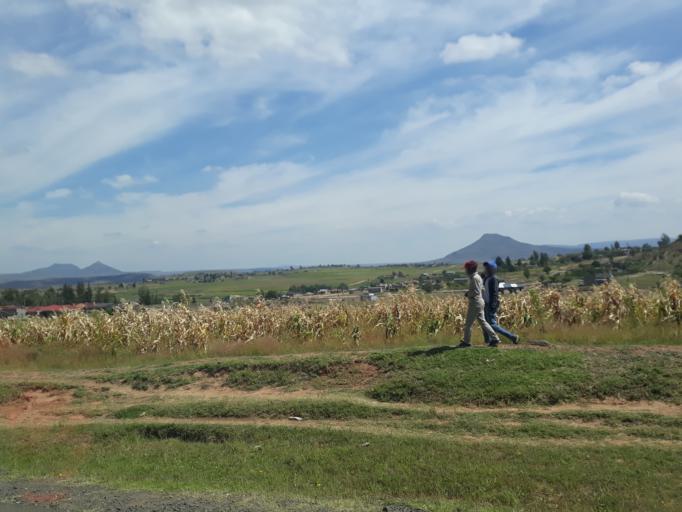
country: LS
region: Mohale's Hoek District
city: Mohale's Hoek
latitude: -30.1059
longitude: 27.4760
